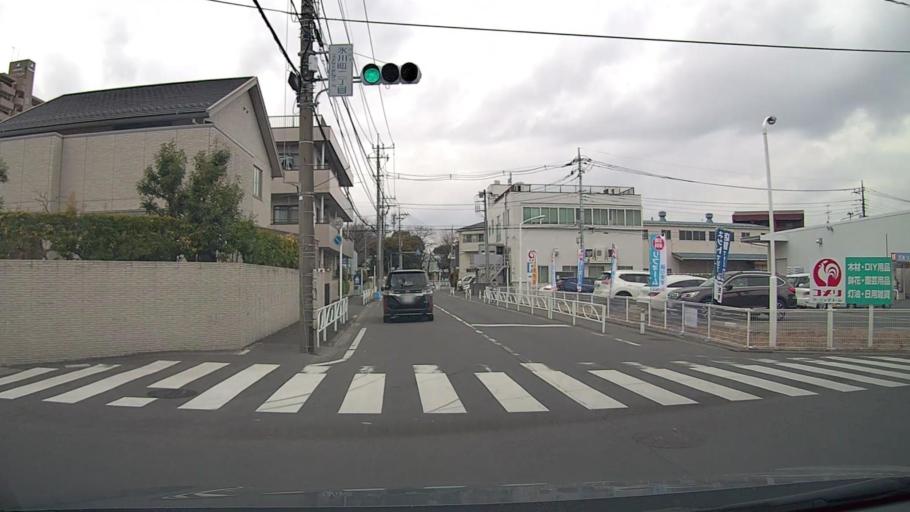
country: JP
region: Saitama
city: Shimotoda
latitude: 35.8094
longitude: 139.6577
